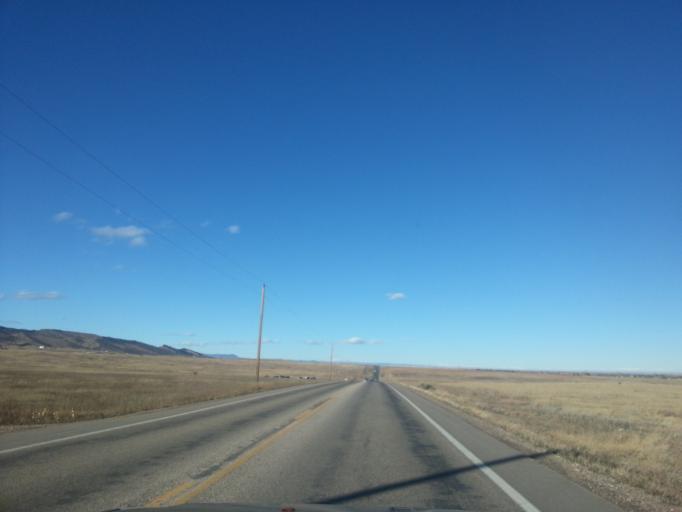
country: US
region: Colorado
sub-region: Larimer County
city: Loveland
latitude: 40.4763
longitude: -105.1157
